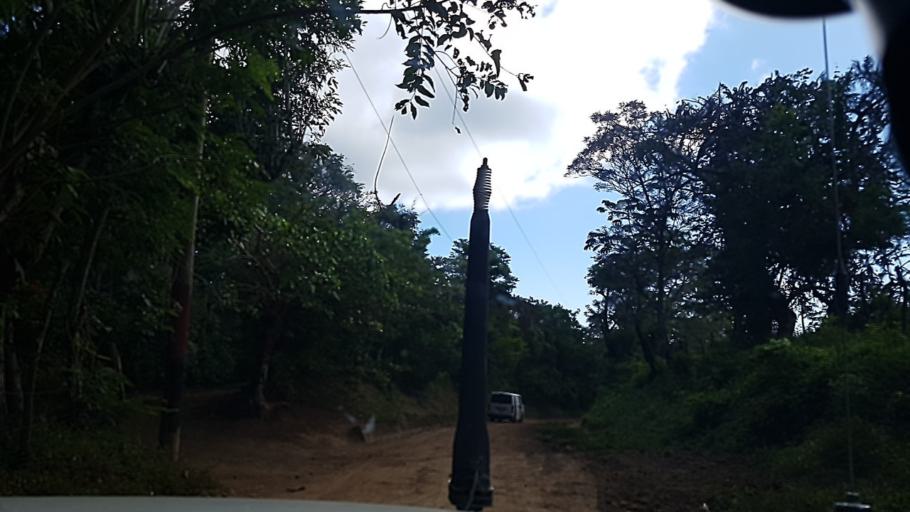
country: NI
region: Carazo
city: La Paz de Oriente
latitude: 11.8252
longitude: -86.1366
